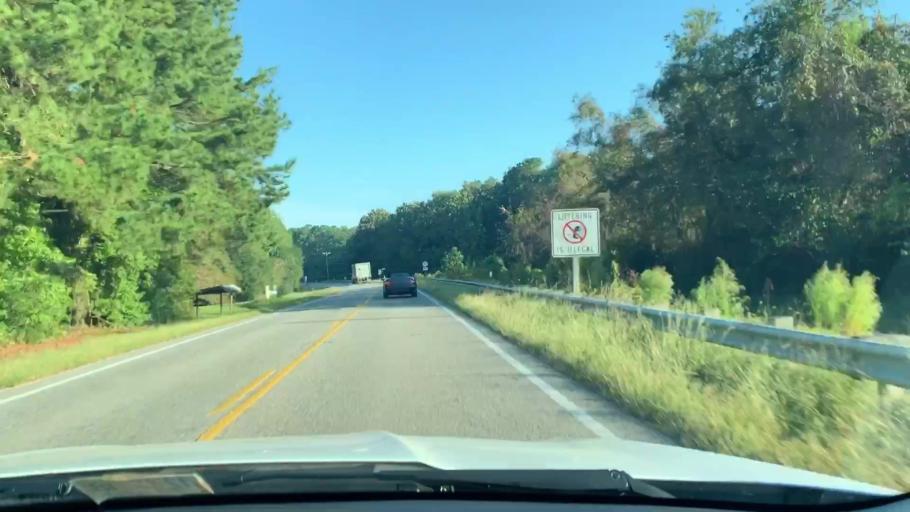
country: US
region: Virginia
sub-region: Middlesex County
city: Deltaville
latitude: 37.5146
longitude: -76.4199
